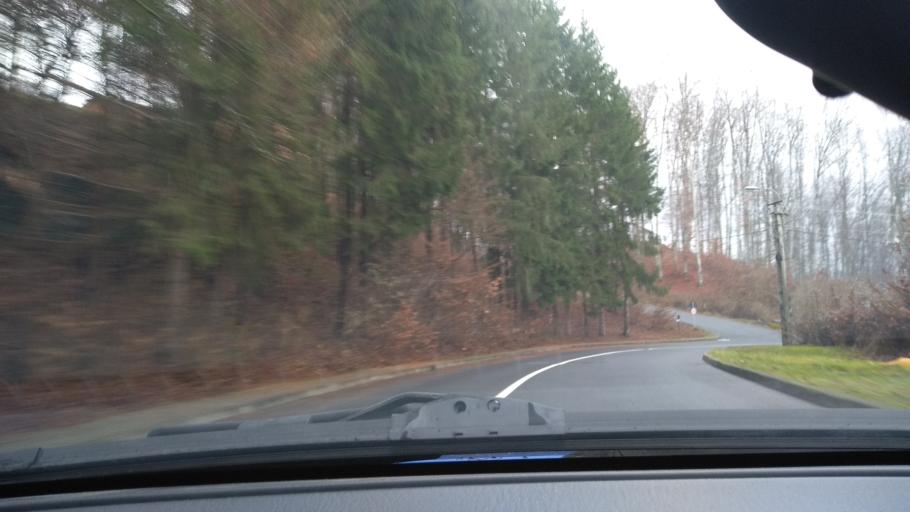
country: RO
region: Mures
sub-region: Oras Sovata
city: Sovata
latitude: 46.5950
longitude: 25.0804
